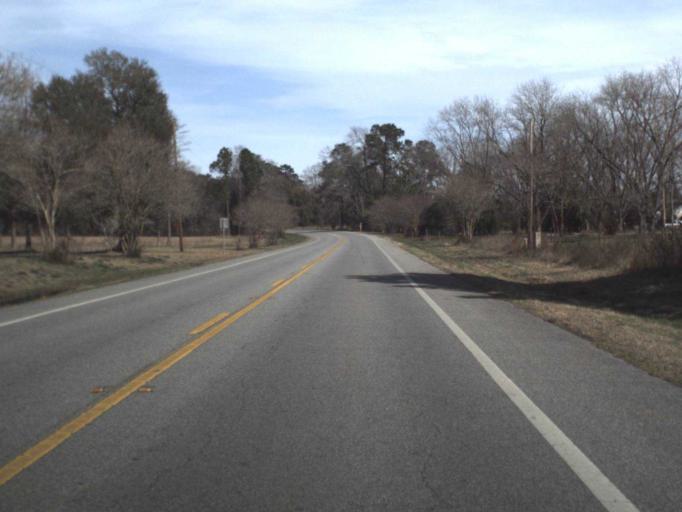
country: US
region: Florida
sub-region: Jackson County
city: Graceville
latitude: 30.9754
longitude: -85.4961
